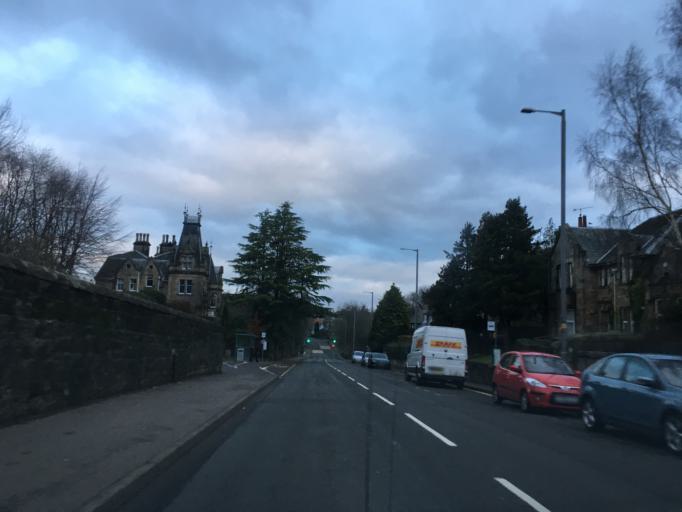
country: GB
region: Scotland
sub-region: Stirling
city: Bannockburn
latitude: 56.0910
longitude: -3.9132
